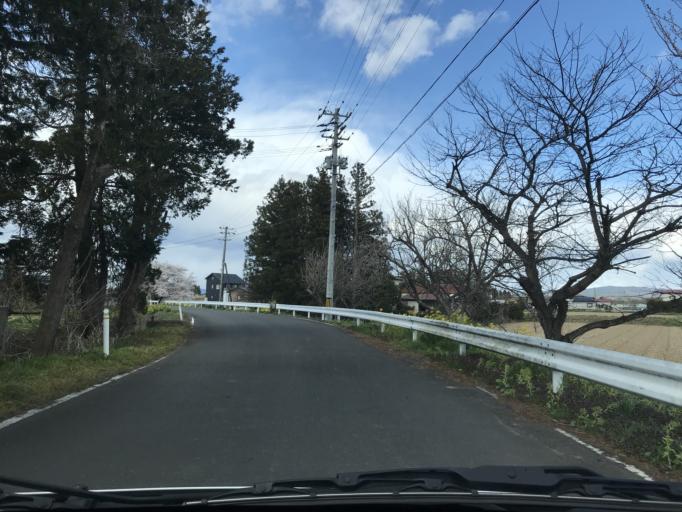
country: JP
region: Miyagi
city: Wakuya
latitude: 38.6485
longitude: 141.2064
